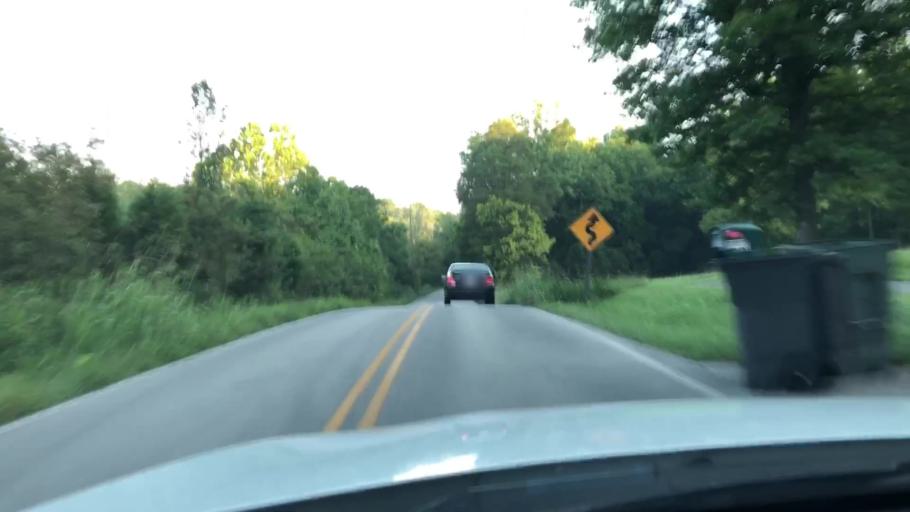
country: US
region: Kentucky
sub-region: Jefferson County
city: Middletown
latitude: 38.1939
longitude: -85.4896
